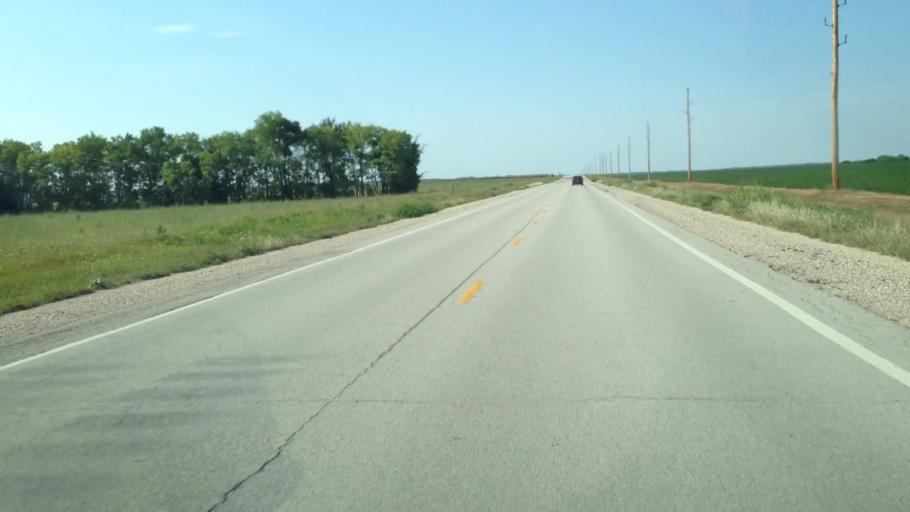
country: US
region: Kansas
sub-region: Anderson County
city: Garnett
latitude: 38.0462
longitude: -95.1696
